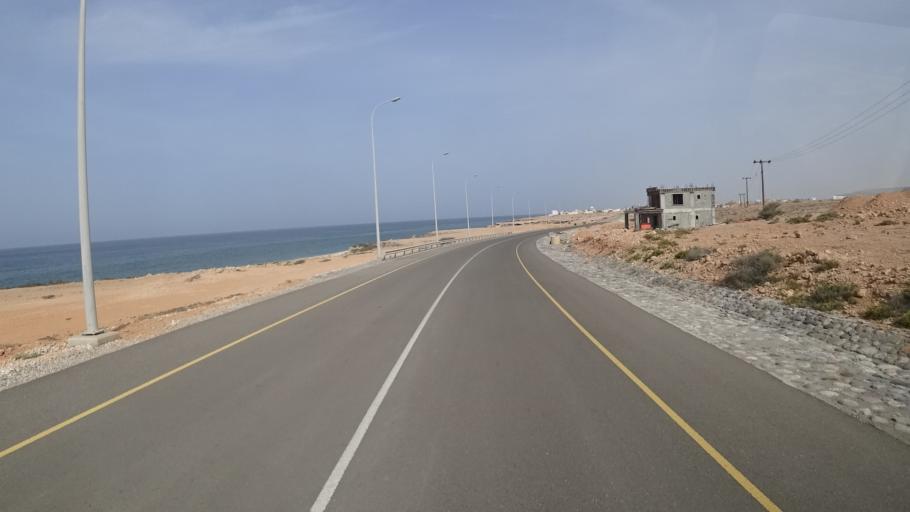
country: OM
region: Ash Sharqiyah
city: Sur
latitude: 22.9981
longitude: 59.1241
